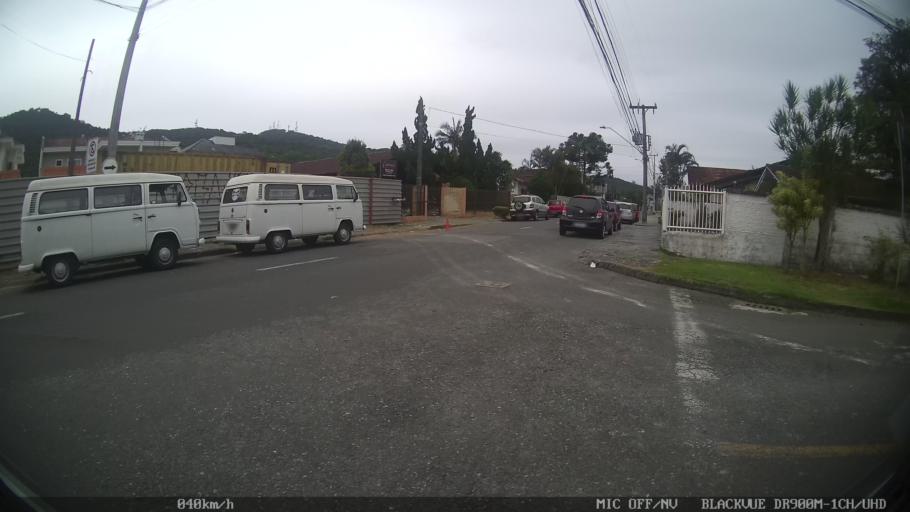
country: BR
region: Santa Catarina
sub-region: Joinville
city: Joinville
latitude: -26.2833
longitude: -48.8352
